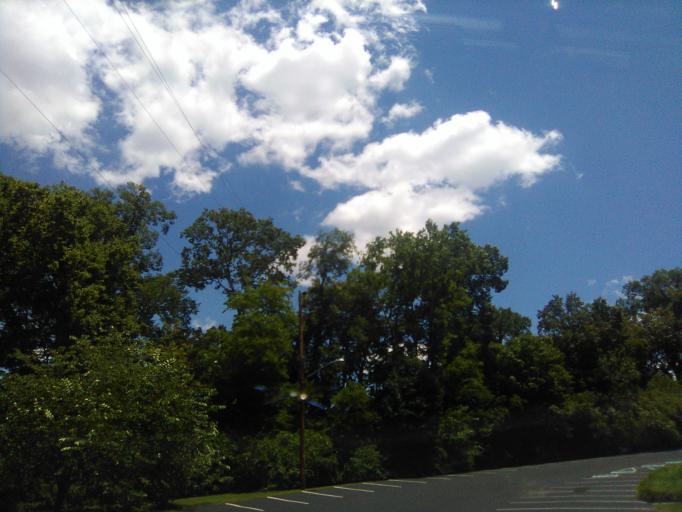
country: US
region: Tennessee
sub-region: Davidson County
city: Belle Meade
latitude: 36.1122
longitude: -86.8541
